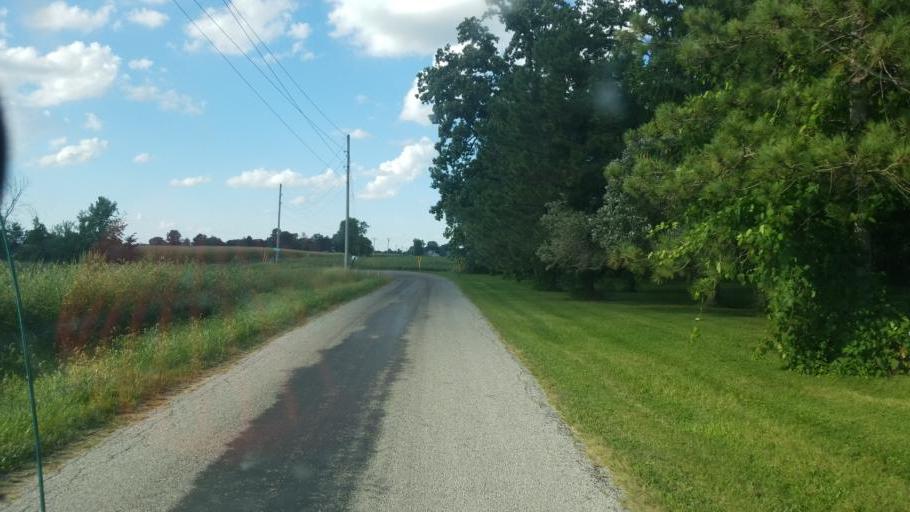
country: US
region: Ohio
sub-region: Marion County
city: Marion
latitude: 40.6442
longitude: -82.9909
